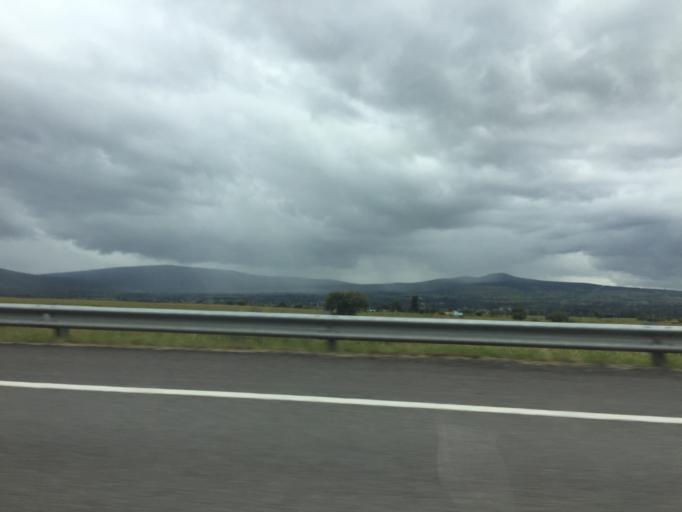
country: MX
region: Jalisco
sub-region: Zapotlanejo
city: La Mezquitera
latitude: 20.5585
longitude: -103.0691
